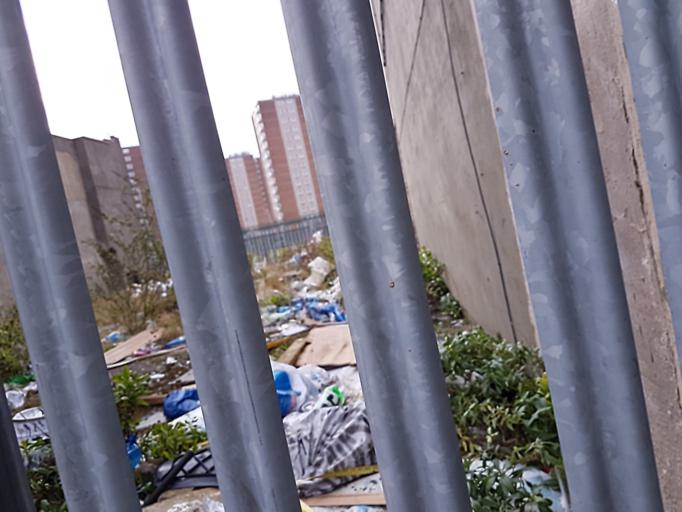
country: GB
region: England
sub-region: North East Lincolnshire
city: Grimsby
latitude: 53.5746
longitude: -0.0700
